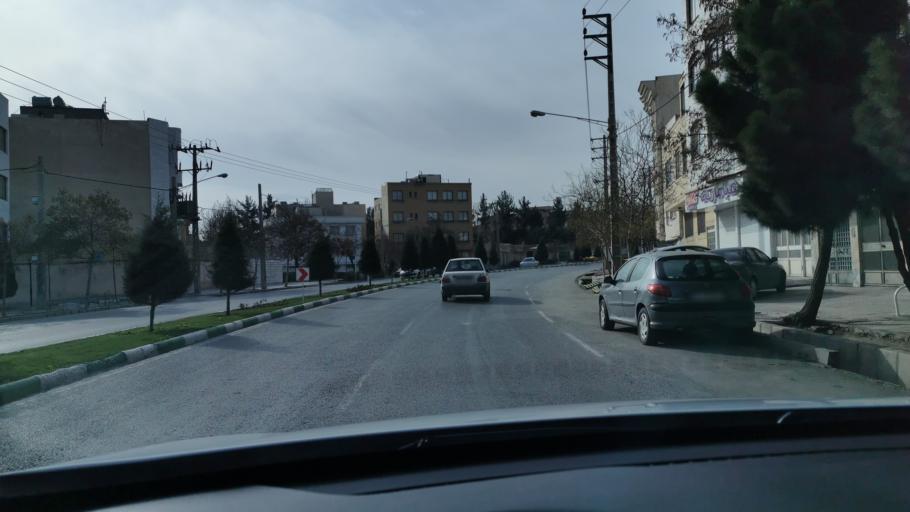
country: IR
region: Razavi Khorasan
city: Mashhad
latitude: 36.3119
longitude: 59.5158
